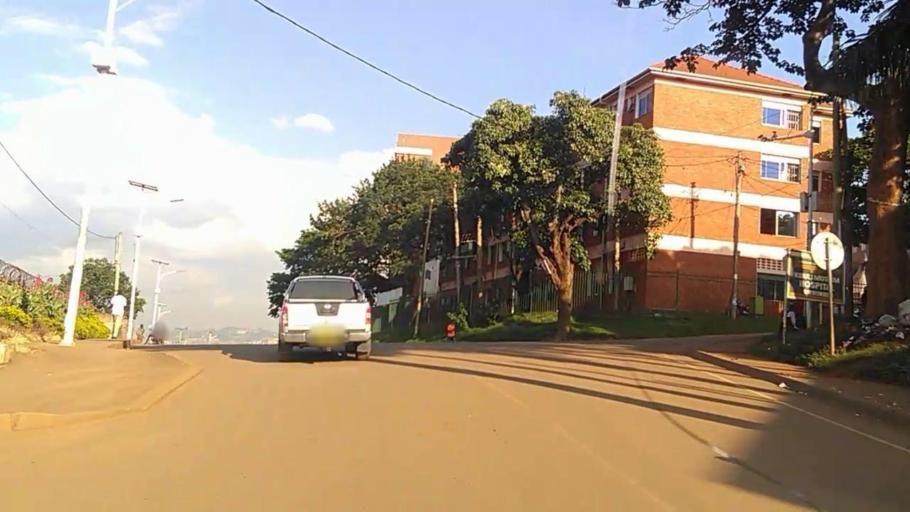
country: UG
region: Central Region
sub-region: Kampala District
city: Kampala
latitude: 0.3085
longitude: 32.5960
